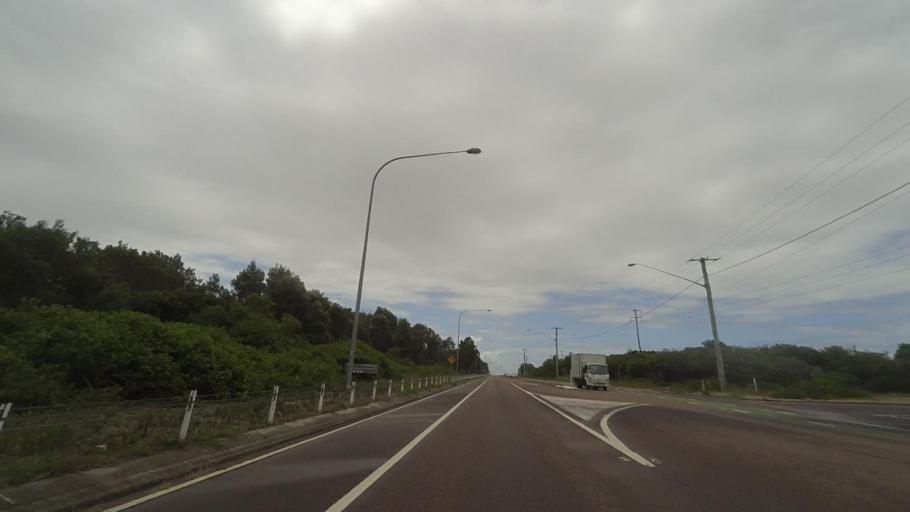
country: AU
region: New South Wales
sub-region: Wyong Shire
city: The Entrance
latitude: -33.3135
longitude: 151.5193
